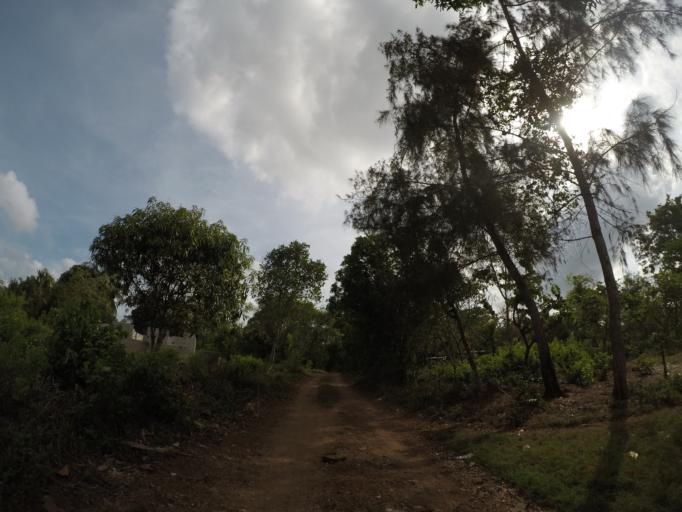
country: TZ
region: Zanzibar Central/South
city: Koani
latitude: -6.2182
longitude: 39.3210
